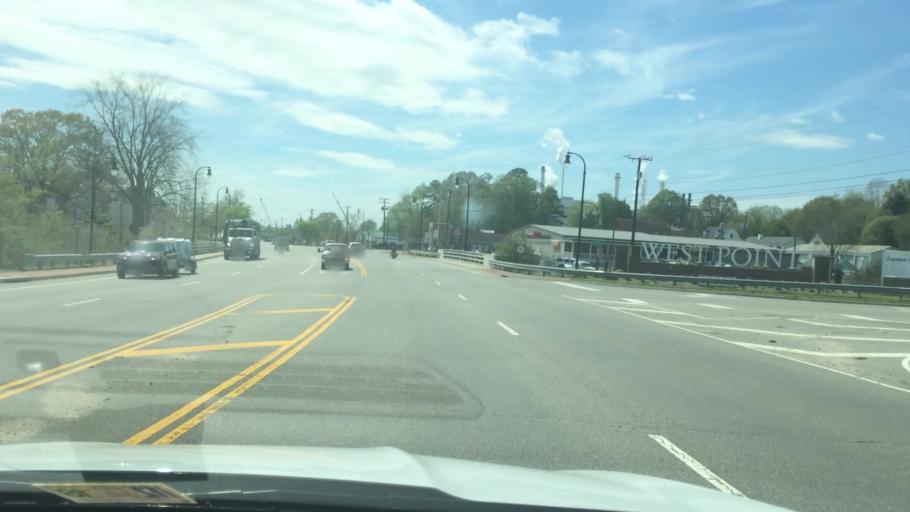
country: US
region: Virginia
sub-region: King William County
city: West Point
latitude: 37.5383
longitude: -76.7946
